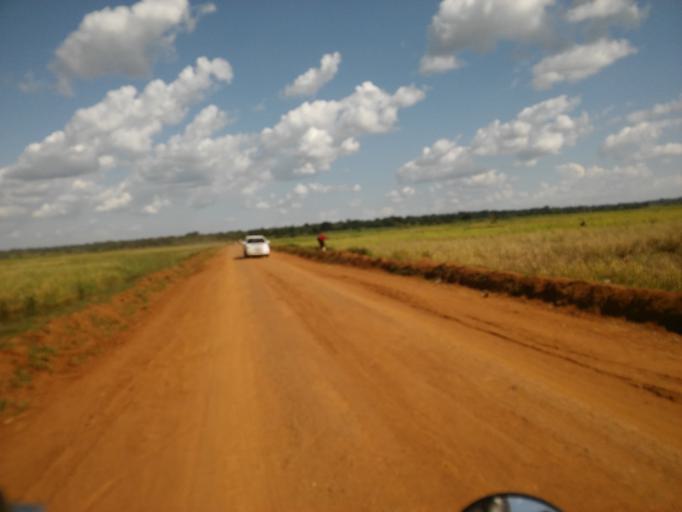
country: UG
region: Eastern Region
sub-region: Pallisa District
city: Pallisa
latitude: 1.1115
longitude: 33.7426
